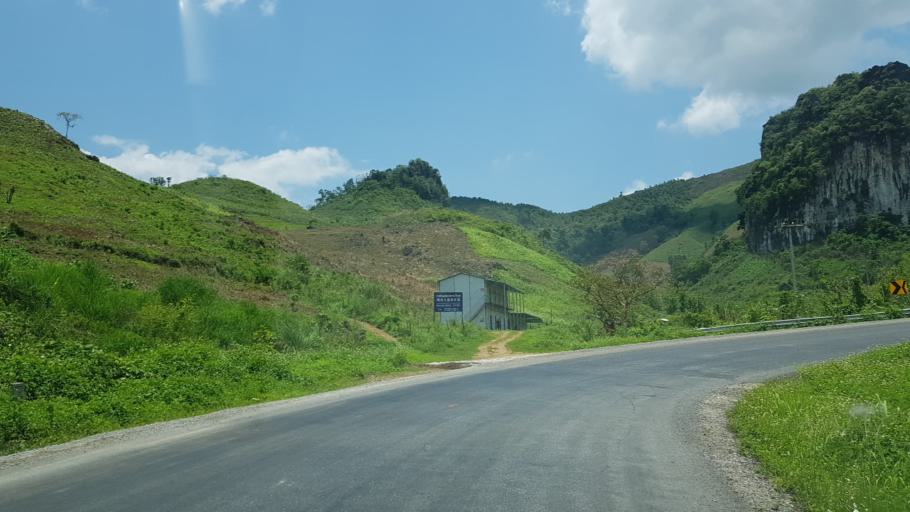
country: LA
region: Vientiane
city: Muang Kasi
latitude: 19.1410
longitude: 102.2911
